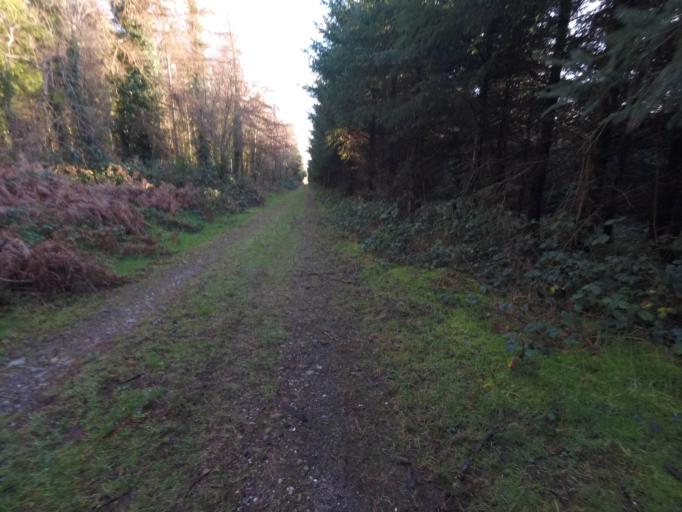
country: IE
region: Munster
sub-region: Waterford
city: Portlaw
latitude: 52.3070
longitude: -7.3548
